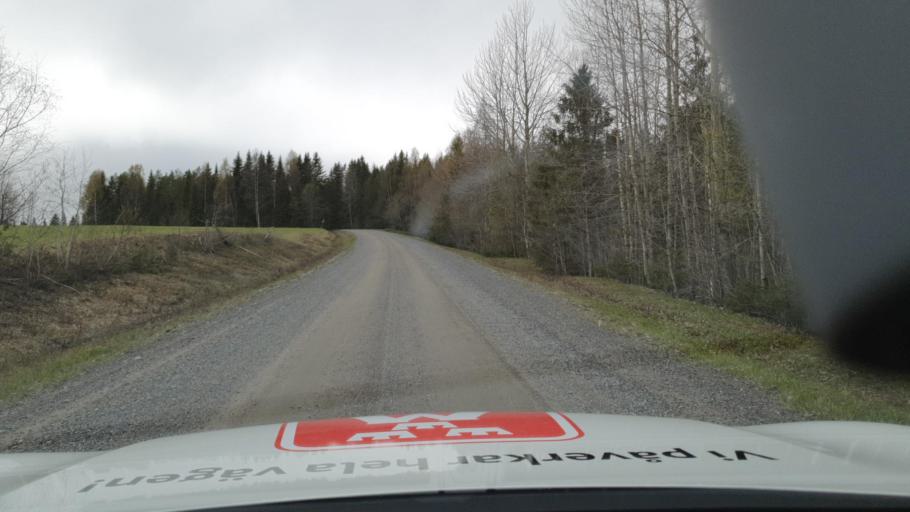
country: SE
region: Vaesterbotten
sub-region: Bjurholms Kommun
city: Bjurholm
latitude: 63.7958
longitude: 19.3380
